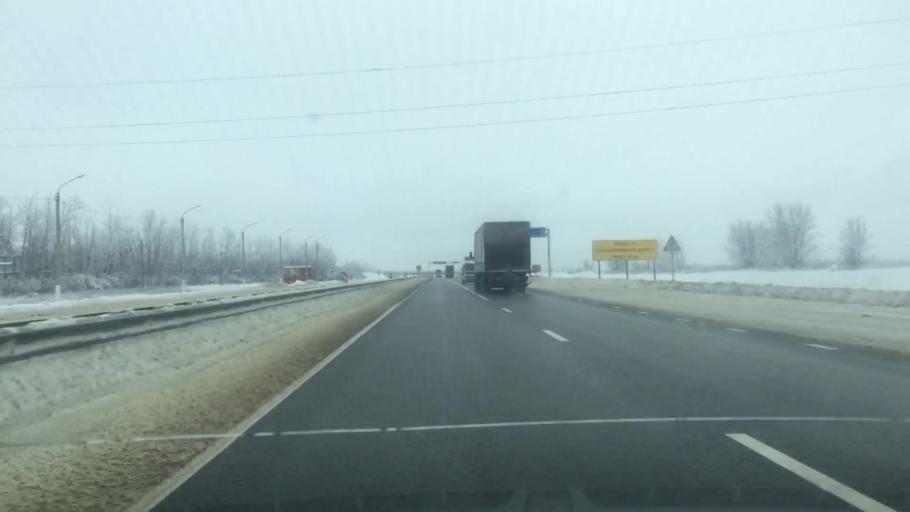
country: RU
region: Tula
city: Kazachka
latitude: 53.3060
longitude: 38.1787
